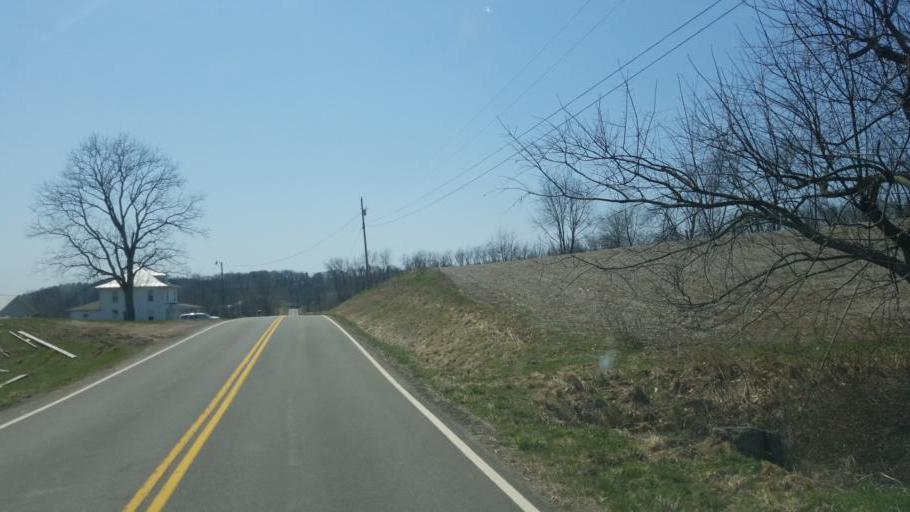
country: US
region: Ohio
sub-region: Ashland County
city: Loudonville
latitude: 40.6855
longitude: -82.2888
